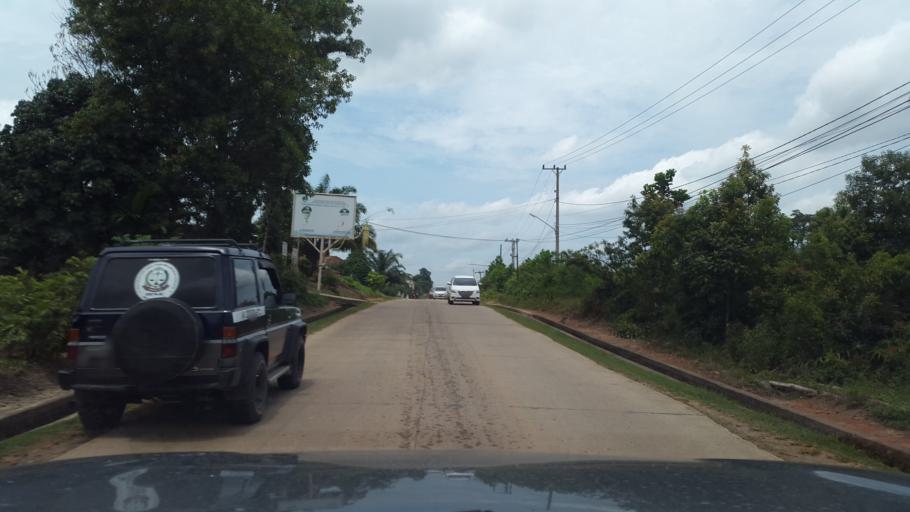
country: ID
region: South Sumatra
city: Gunungmegang Dalam
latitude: -3.2996
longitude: 103.8560
